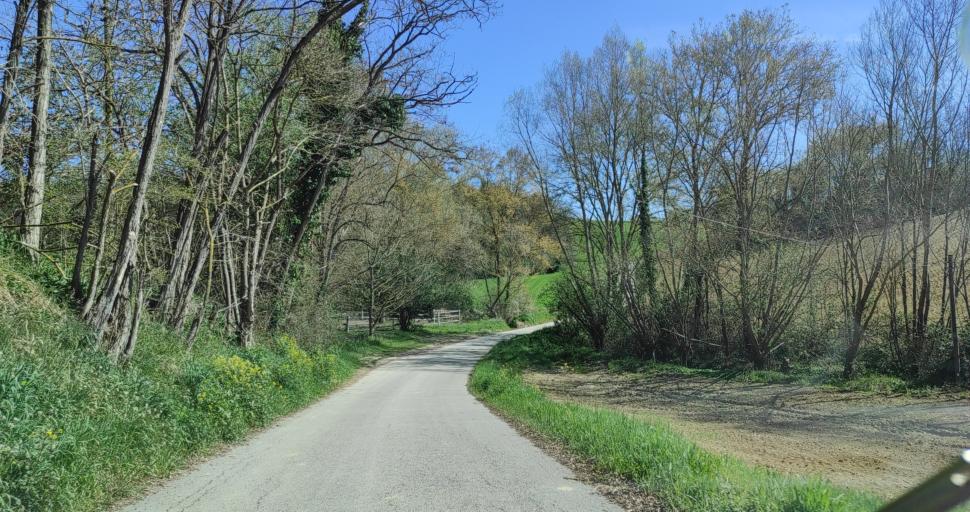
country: IT
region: The Marches
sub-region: Provincia di Macerata
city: Piediripa
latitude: 43.3133
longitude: 13.5003
